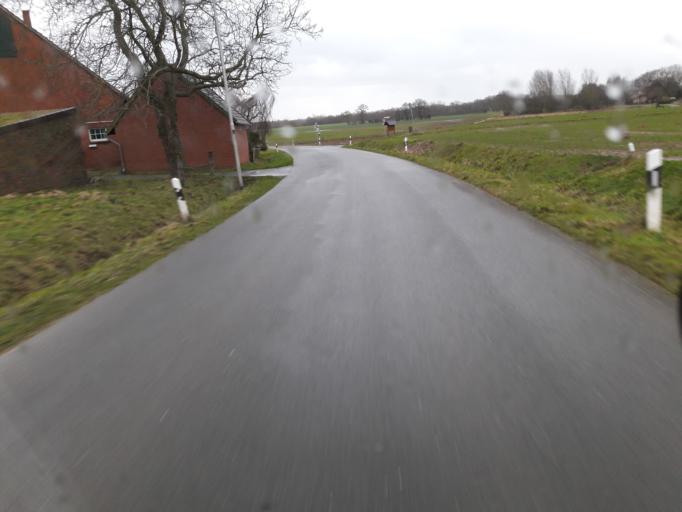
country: DE
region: Lower Saxony
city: Raddestorf
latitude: 52.4439
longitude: 8.9879
